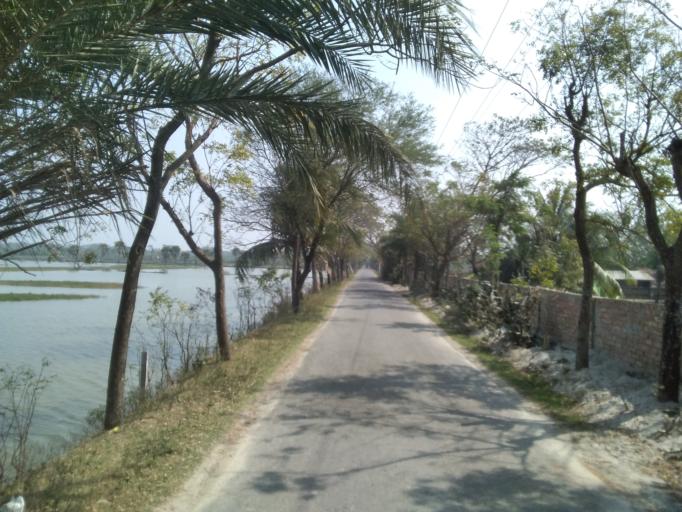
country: IN
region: West Bengal
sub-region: North 24 Parganas
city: Taki
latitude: 22.5931
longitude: 88.9874
